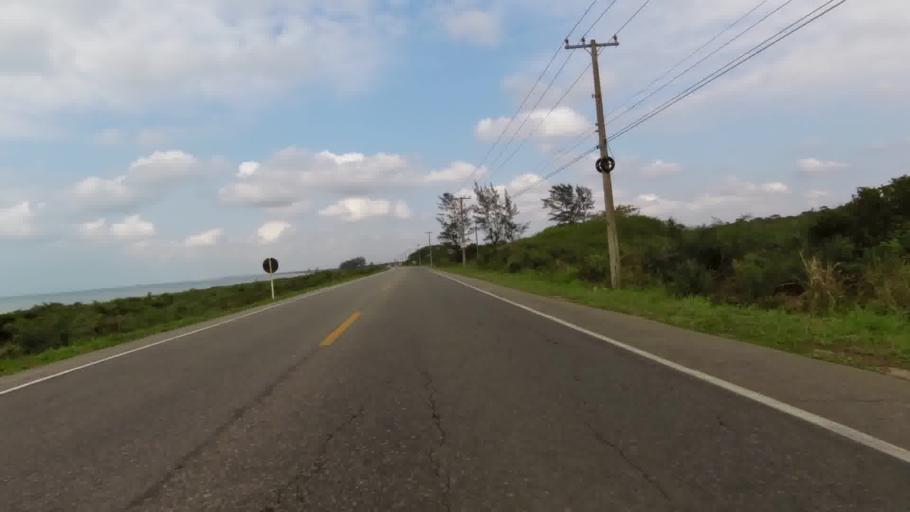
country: BR
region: Espirito Santo
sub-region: Itapemirim
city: Itapemirim
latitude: -20.9271
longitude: -40.7969
